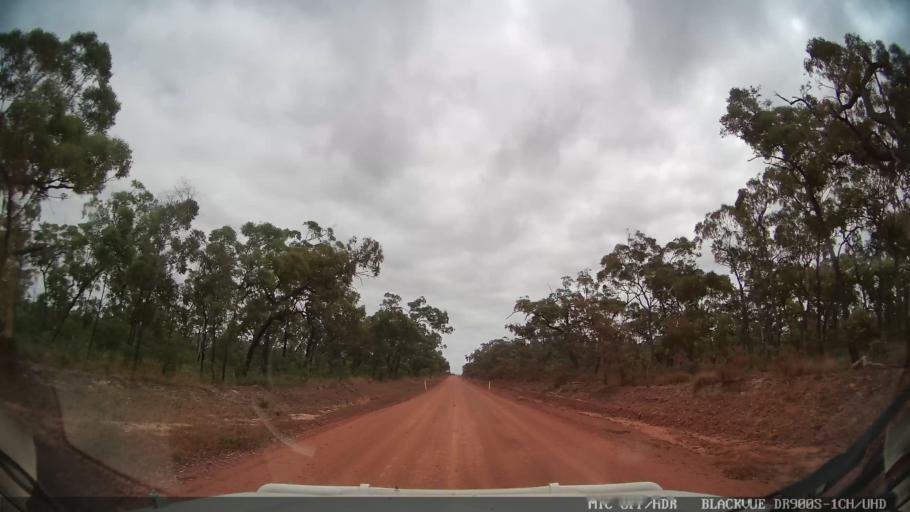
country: AU
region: Queensland
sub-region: Cook
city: Cooktown
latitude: -15.2659
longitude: 144.9490
